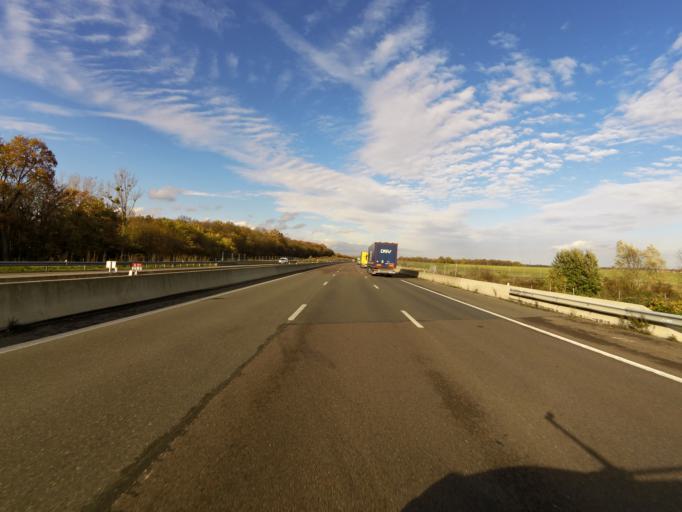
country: FR
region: Bourgogne
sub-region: Departement de la Cote-d'Or
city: Gevrey-Chambertin
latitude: 47.1993
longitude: 4.9965
